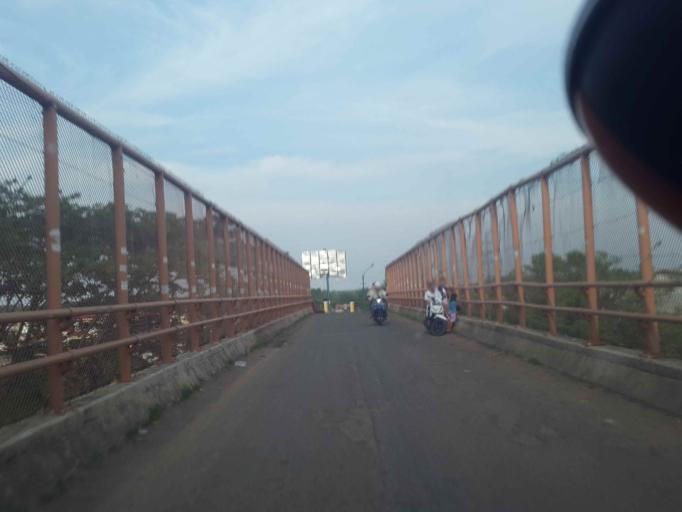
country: ID
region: Banten
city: Serang
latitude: -6.0638
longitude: 106.1242
